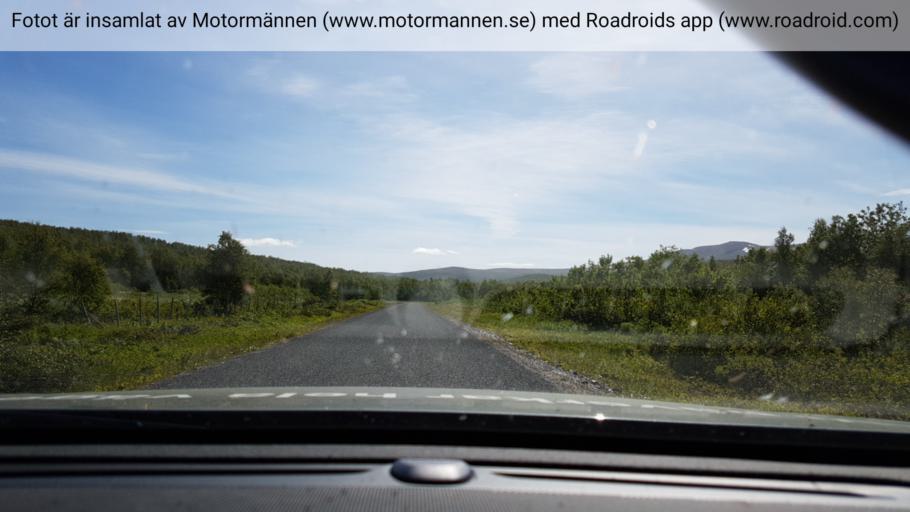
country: NO
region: Nordland
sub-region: Hattfjelldal
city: Hattfjelldal
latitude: 65.4241
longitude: 14.6584
